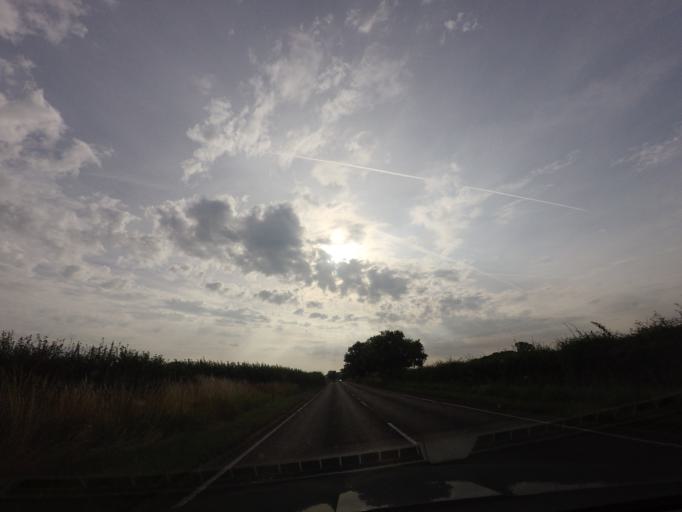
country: GB
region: England
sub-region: Staffordshire
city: Wheaton Aston
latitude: 52.6941
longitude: -2.2118
